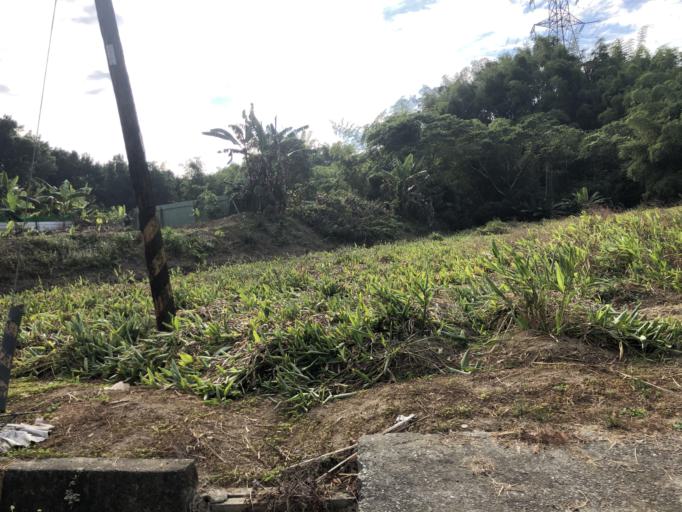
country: TW
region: Taiwan
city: Yujing
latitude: 23.0202
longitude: 120.4142
